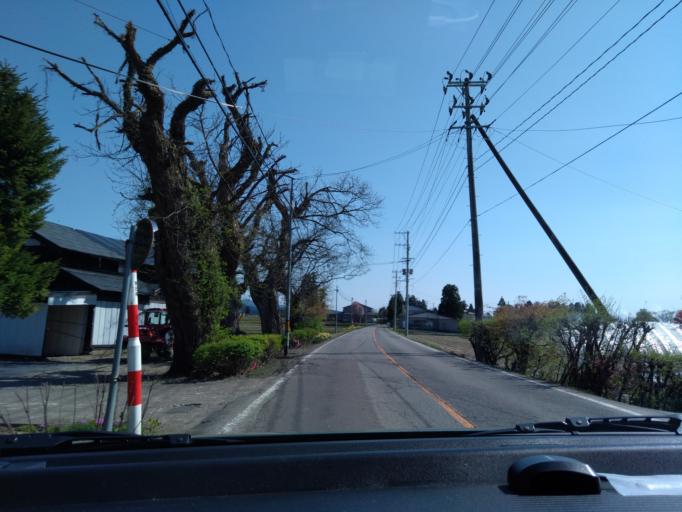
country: JP
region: Akita
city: Kakunodatemachi
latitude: 39.4932
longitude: 140.5941
